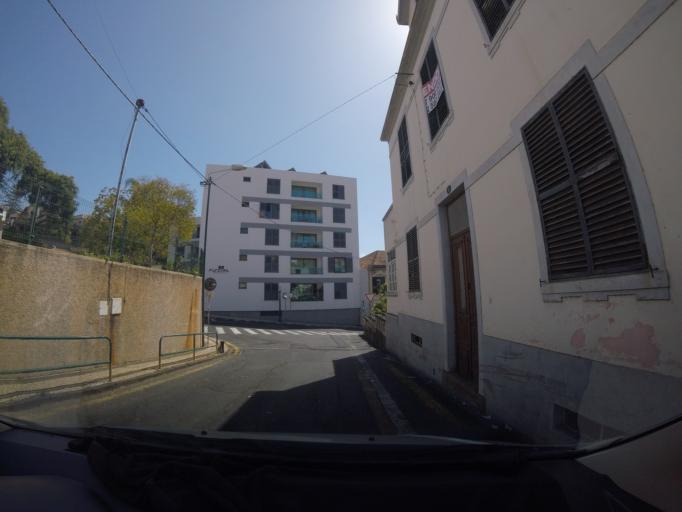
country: PT
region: Madeira
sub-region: Funchal
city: Nossa Senhora do Monte
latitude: 32.6539
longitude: -16.9054
